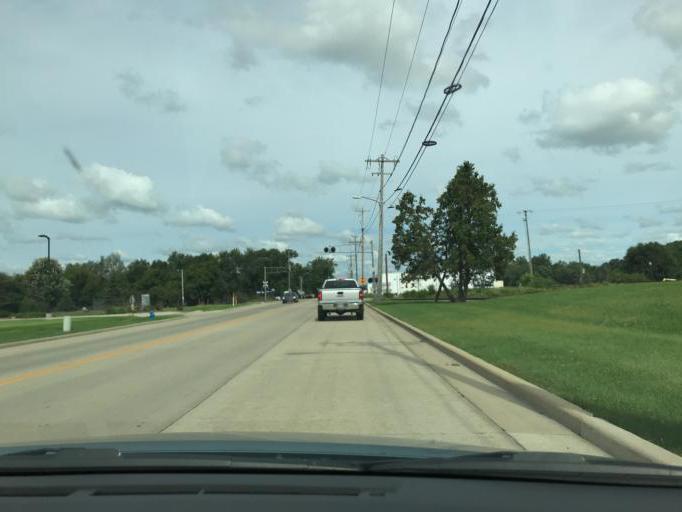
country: US
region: Wisconsin
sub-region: Racine County
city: Burlington
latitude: 42.6671
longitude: -88.2659
